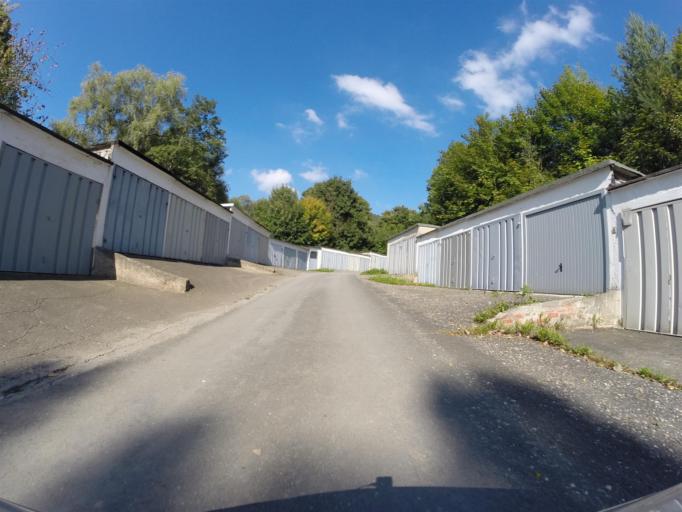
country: DE
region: Thuringia
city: Zollnitz
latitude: 50.8906
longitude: 11.6340
